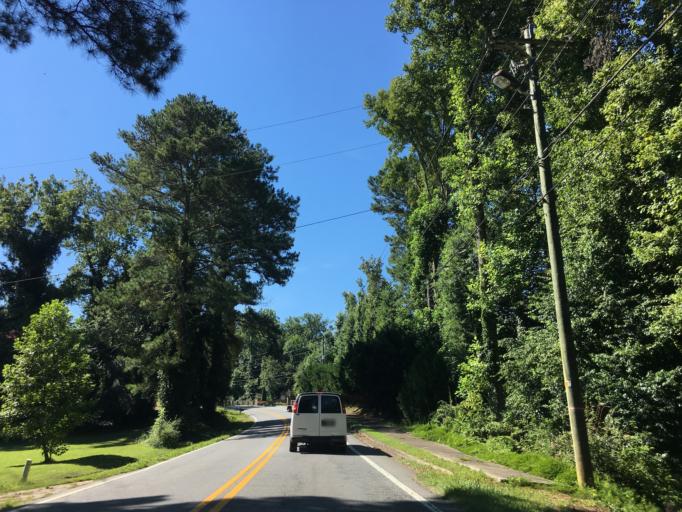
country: US
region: Georgia
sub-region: Fulton County
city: Milton
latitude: 34.1422
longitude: -84.2868
